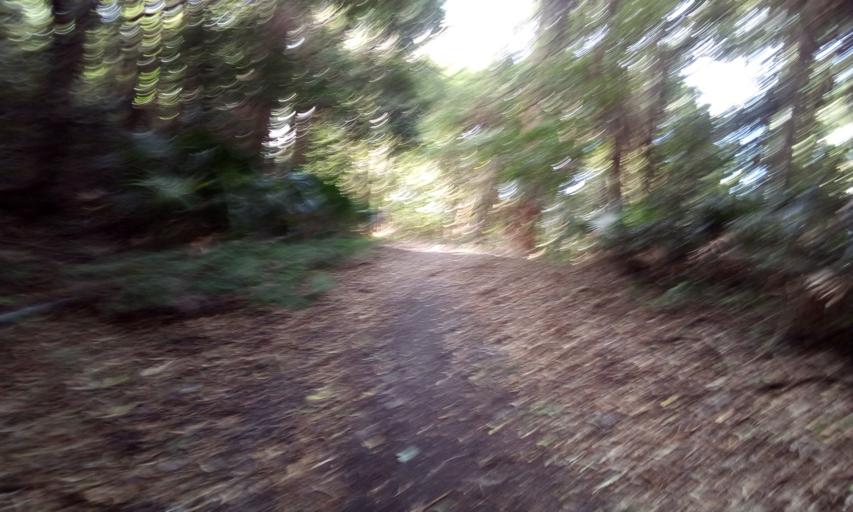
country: AU
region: New South Wales
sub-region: Wollongong
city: Cordeaux Heights
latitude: -34.4407
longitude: 150.8132
